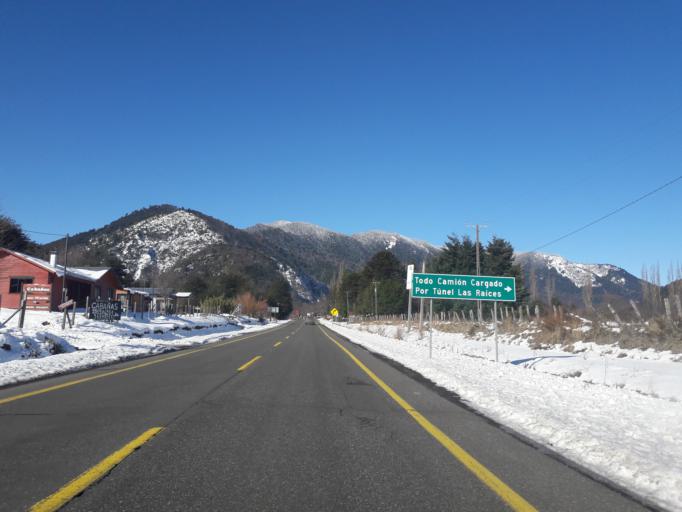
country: CL
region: Araucania
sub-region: Provincia de Cautin
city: Vilcun
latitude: -38.4777
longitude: -71.5421
